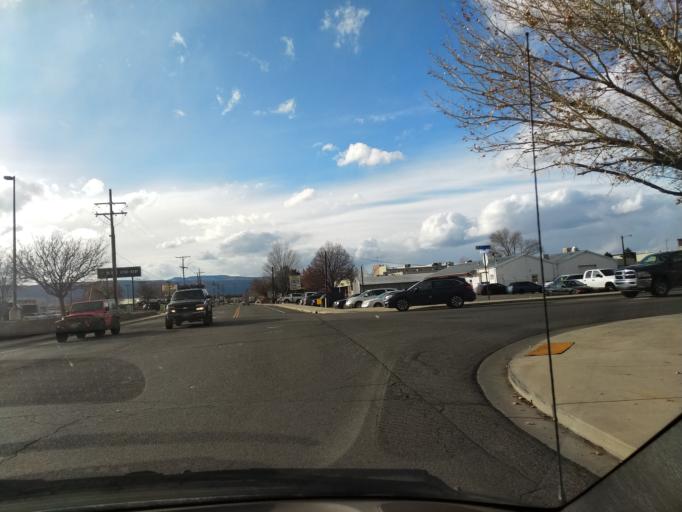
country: US
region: Colorado
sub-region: Mesa County
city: Grand Junction
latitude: 39.0810
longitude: -108.5799
